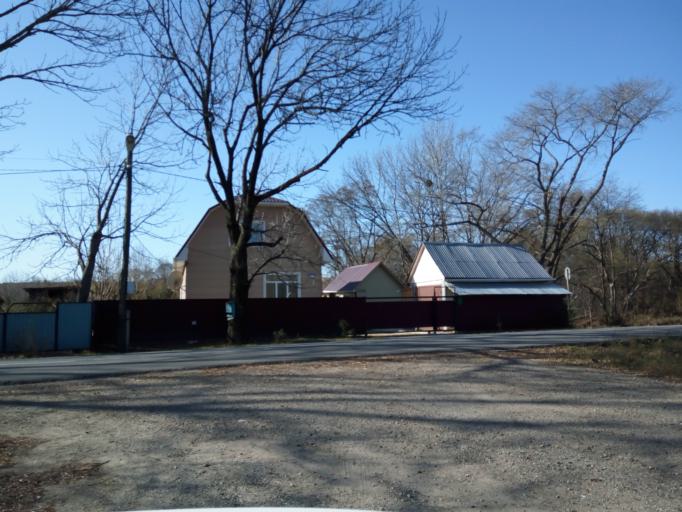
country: RU
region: Primorskiy
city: Dal'nerechensk
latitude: 45.9416
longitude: 133.6887
